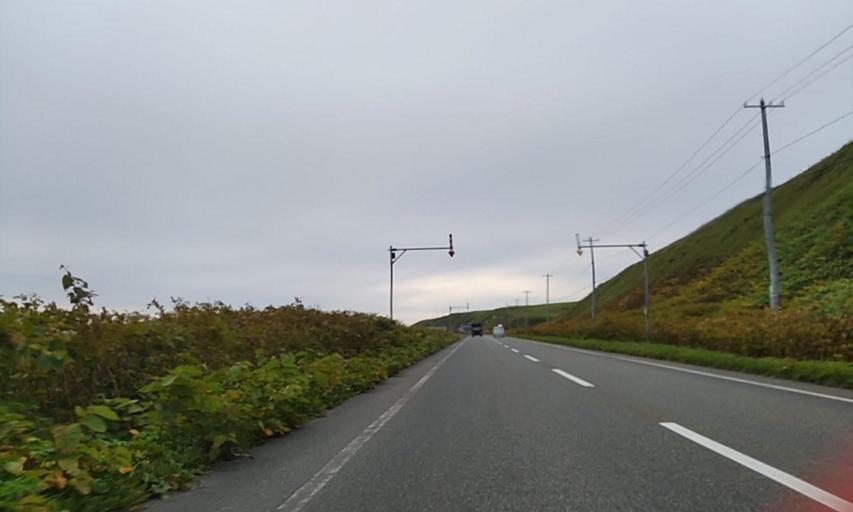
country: JP
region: Hokkaido
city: Makubetsu
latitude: 45.3880
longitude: 142.0737
